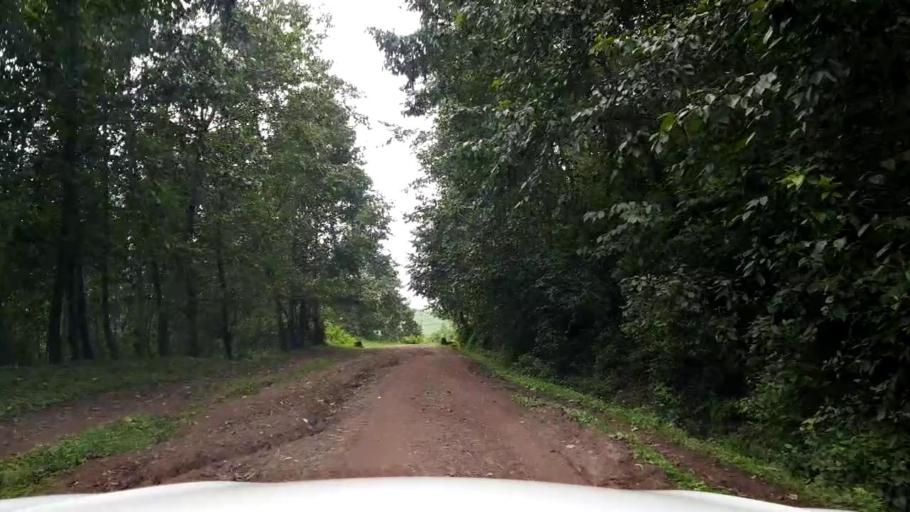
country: RW
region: Western Province
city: Gisenyi
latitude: -1.6543
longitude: 29.4160
